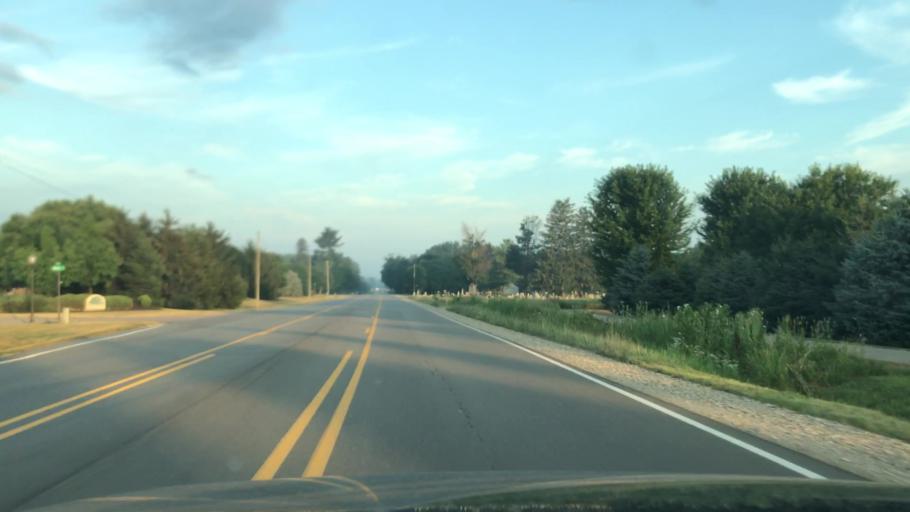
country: US
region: Michigan
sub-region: Ottawa County
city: Zeeland
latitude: 42.7833
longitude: -85.9722
